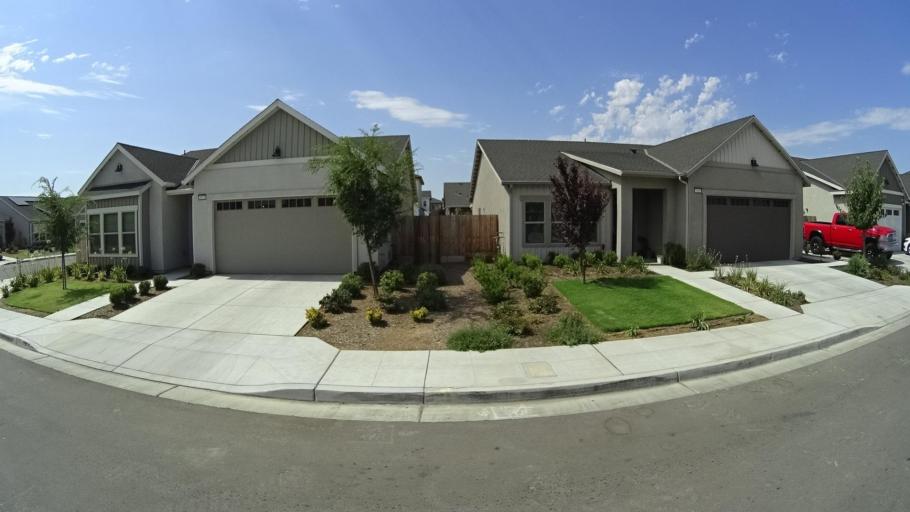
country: US
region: California
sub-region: Fresno County
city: Tarpey Village
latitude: 36.7861
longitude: -119.6649
